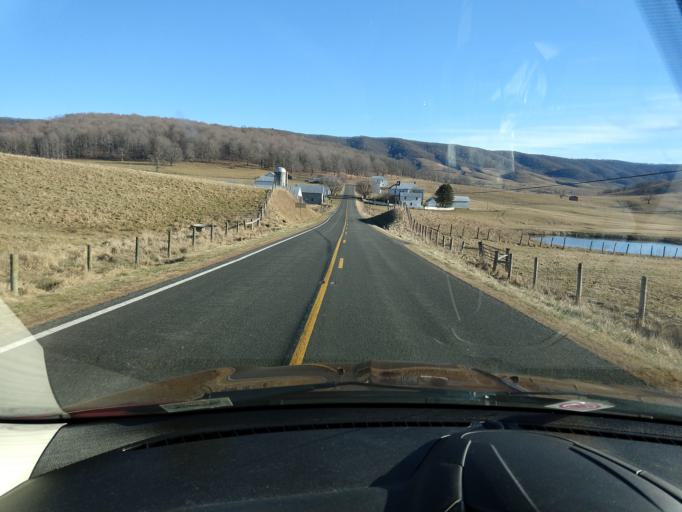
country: US
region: Virginia
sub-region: Highland County
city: Monterey
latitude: 38.4336
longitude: -79.6359
